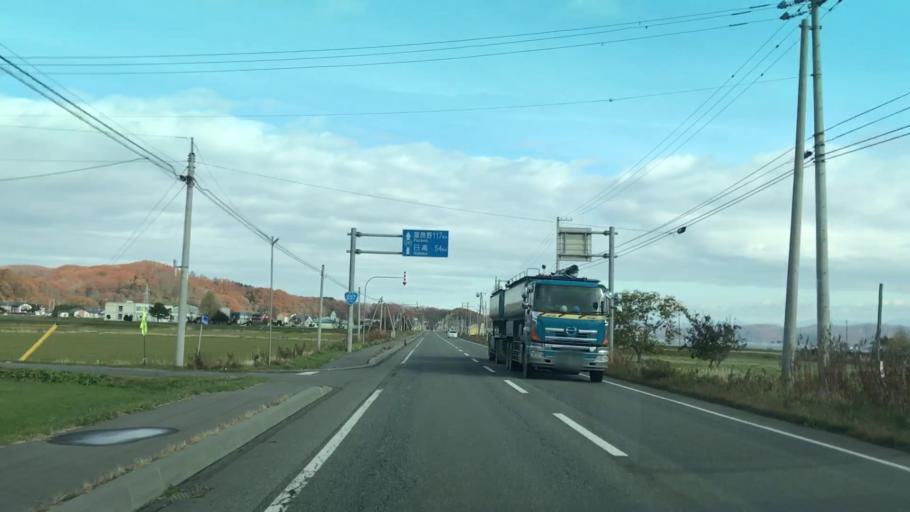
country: JP
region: Hokkaido
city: Shizunai-furukawacho
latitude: 42.5520
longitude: 142.0728
